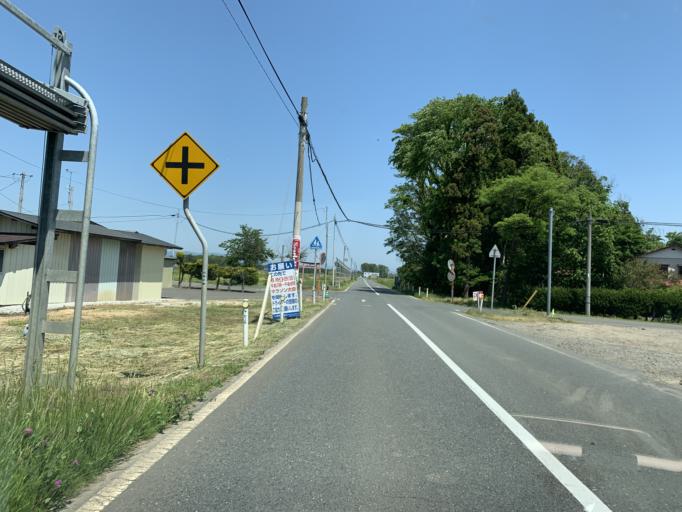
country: JP
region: Iwate
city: Kitakami
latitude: 39.2546
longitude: 141.0651
